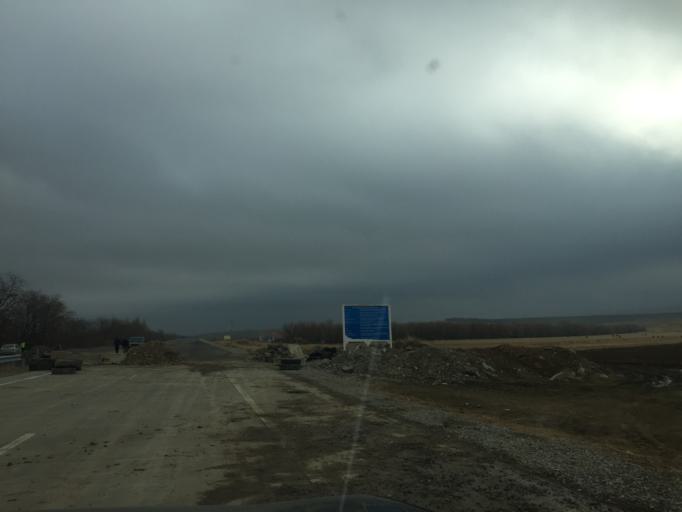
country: KZ
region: Ongtustik Qazaqstan
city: Kokterek
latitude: 42.5530
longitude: 70.1506
